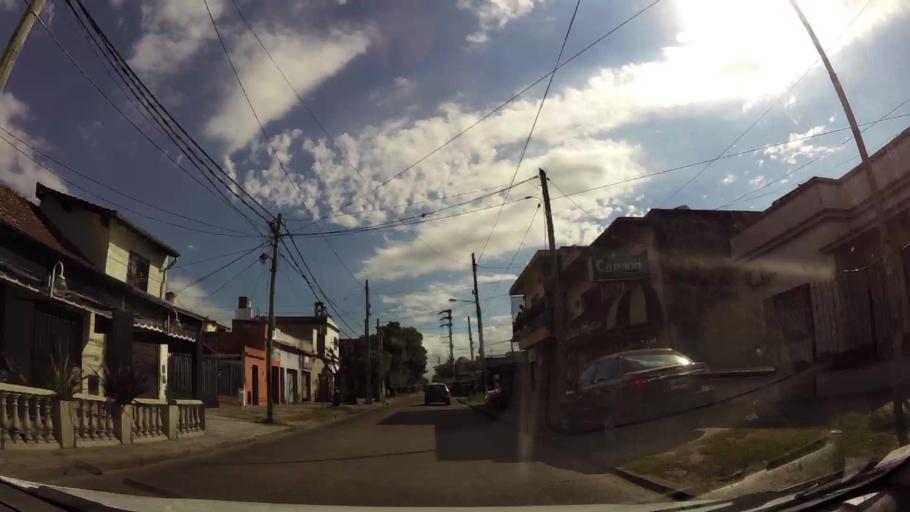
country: AR
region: Buenos Aires
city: San Justo
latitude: -34.6562
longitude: -58.5801
